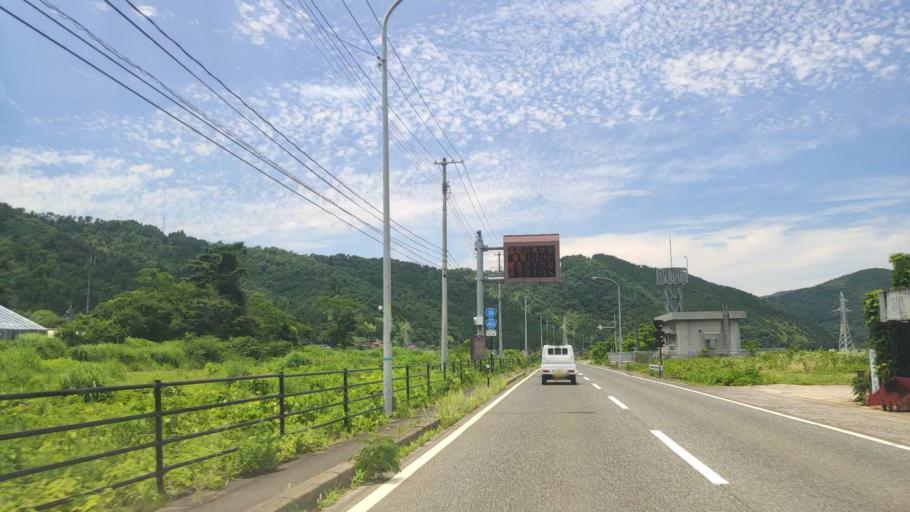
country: JP
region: Tottori
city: Tottori
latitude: 35.3517
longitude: 134.3871
